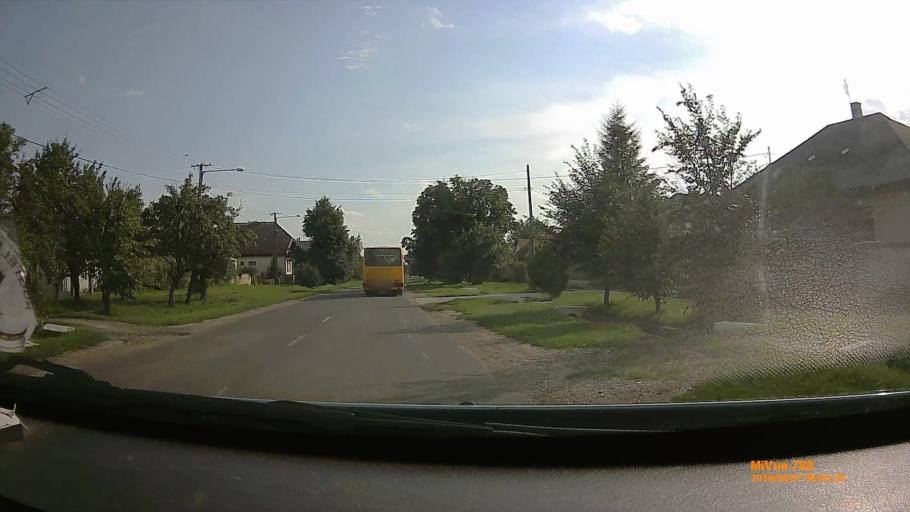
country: HU
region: Borsod-Abauj-Zemplen
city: Encs
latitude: 48.3819
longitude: 21.2157
